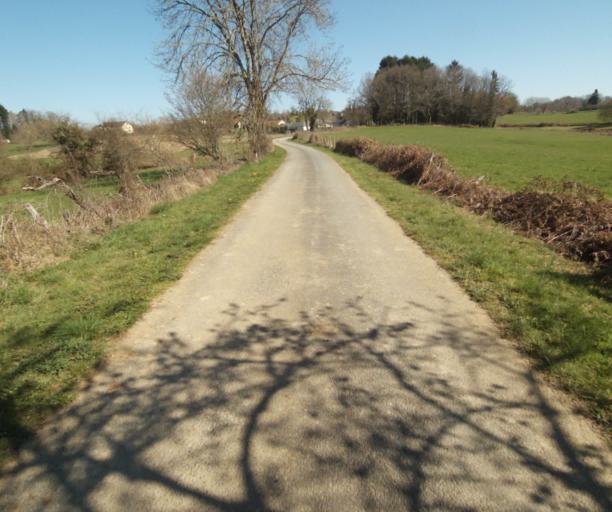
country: FR
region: Limousin
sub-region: Departement de la Correze
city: Saint-Mexant
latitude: 45.3042
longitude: 1.6004
